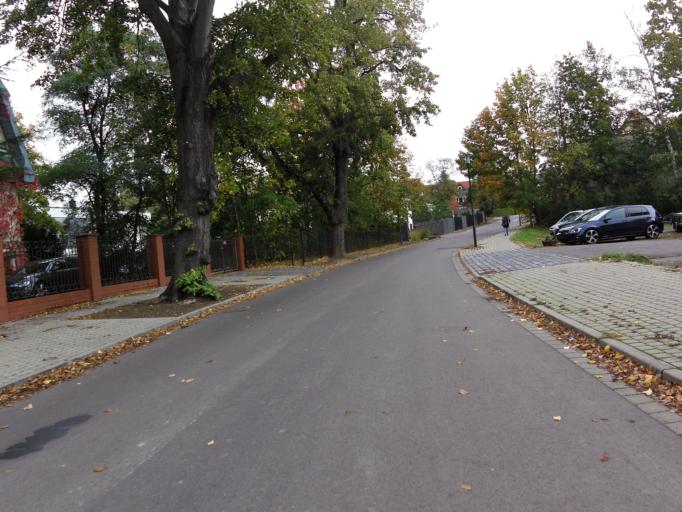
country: DE
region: Saxony
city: Markkleeberg
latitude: 51.2845
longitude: 12.3614
